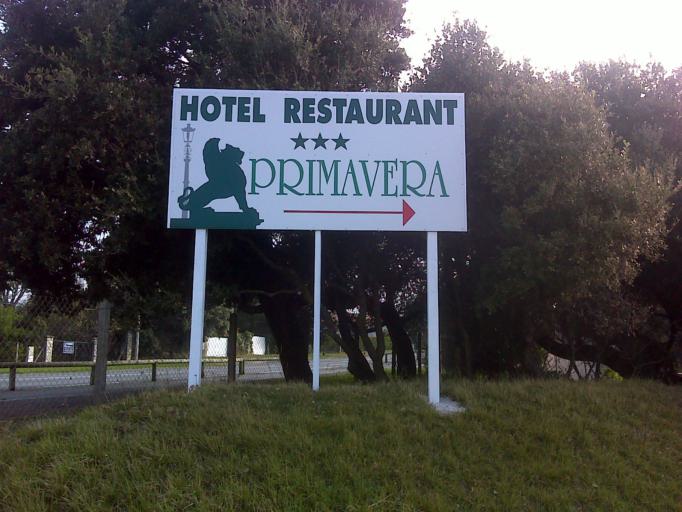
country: FR
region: Poitou-Charentes
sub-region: Departement de la Charente-Maritime
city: Saint-Palais-sur-Mer
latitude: 45.6473
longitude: -1.1100
